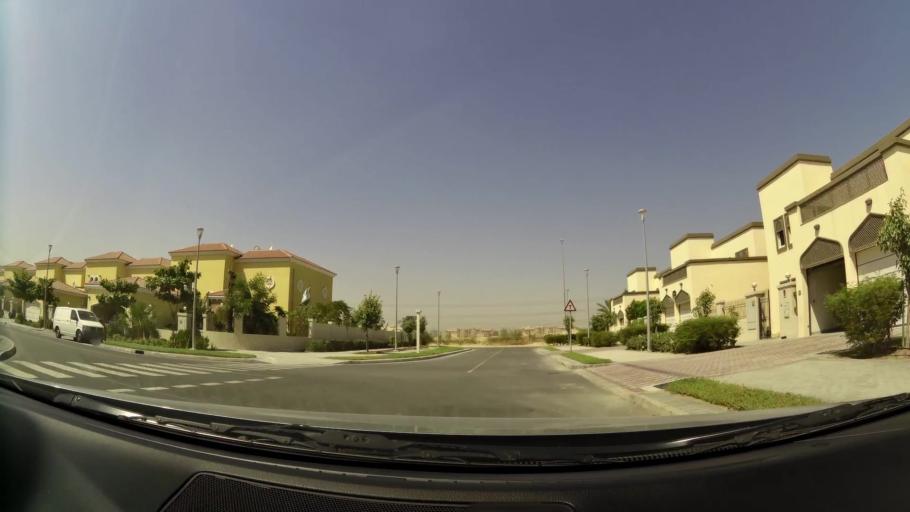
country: AE
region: Dubai
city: Dubai
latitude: 25.0471
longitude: 55.1501
